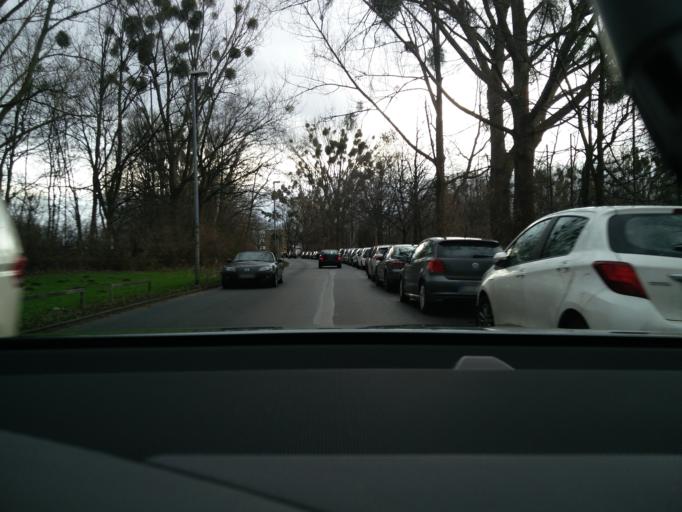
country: DE
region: Lower Saxony
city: Hannover
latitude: 52.3570
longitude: 9.7248
